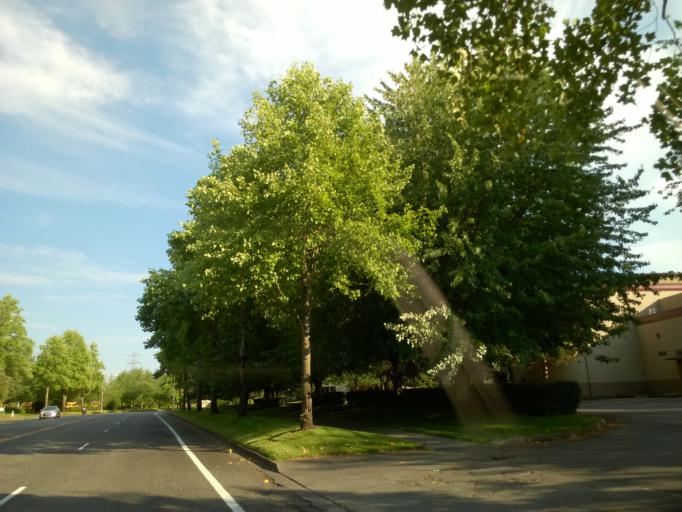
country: US
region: Washington
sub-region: King County
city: Woodinville
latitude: 47.7639
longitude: -122.1774
